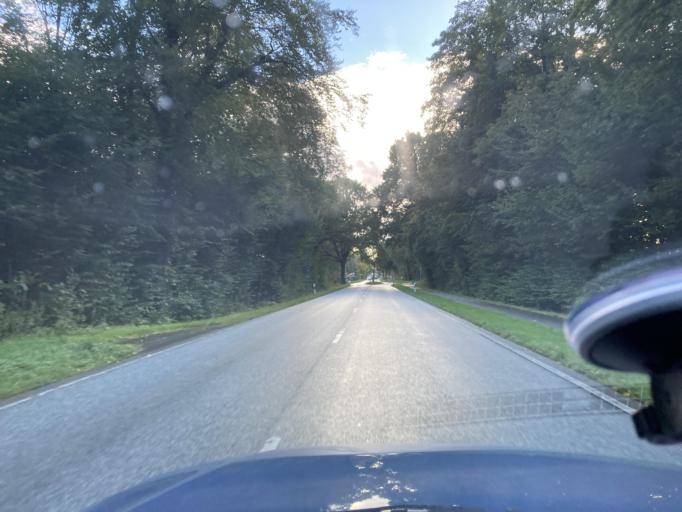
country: DE
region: Schleswig-Holstein
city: Elsdorf-Westermuhlen
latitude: 54.2609
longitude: 9.5394
